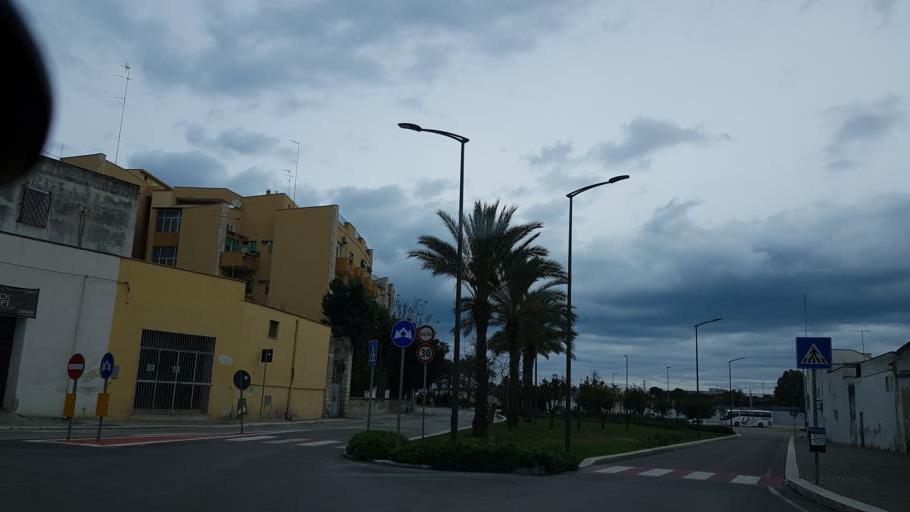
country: IT
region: Apulia
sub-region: Provincia di Brindisi
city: Brindisi
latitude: 40.6320
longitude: 17.9463
